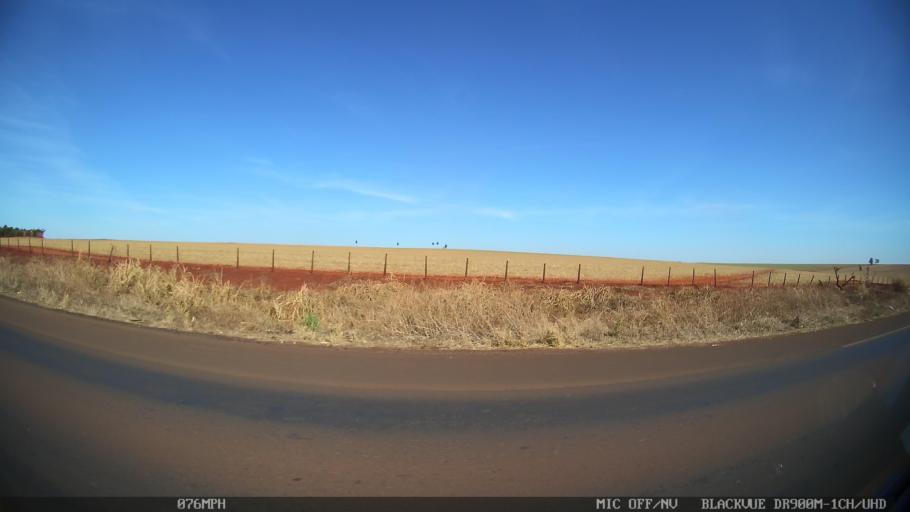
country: BR
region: Sao Paulo
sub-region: Sao Joaquim Da Barra
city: Sao Joaquim da Barra
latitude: -20.5107
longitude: -47.9080
